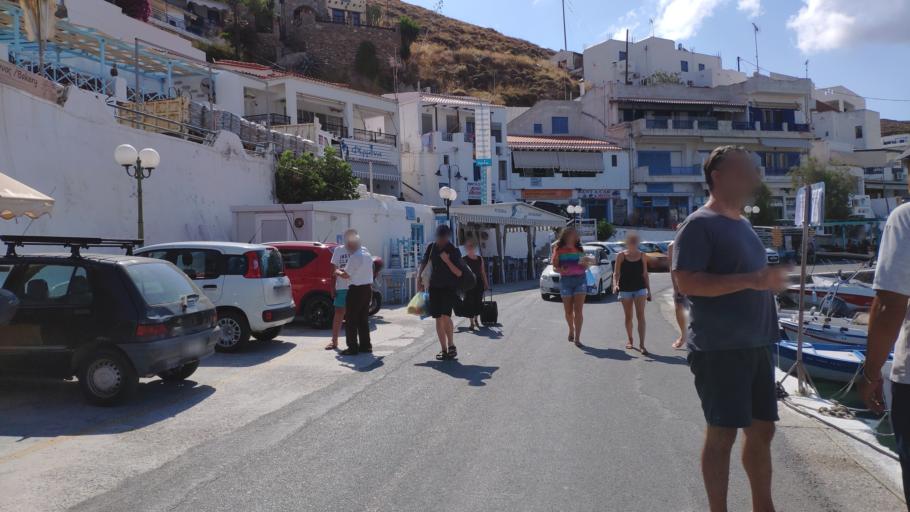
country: GR
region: South Aegean
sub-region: Nomos Kykladon
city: Kythnos
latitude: 37.3900
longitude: 24.3977
